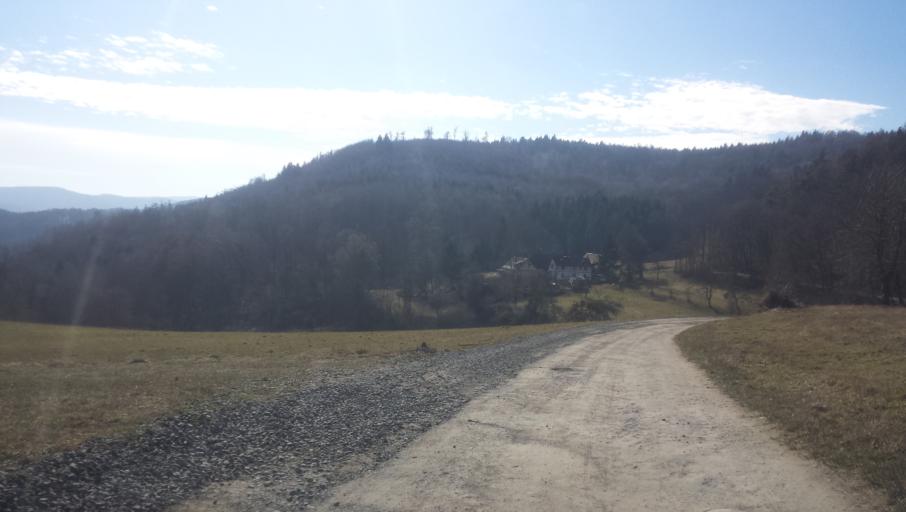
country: DE
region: Hesse
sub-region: Regierungsbezirk Darmstadt
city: Frankisch-Crumbach
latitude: 49.7484
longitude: 8.8242
